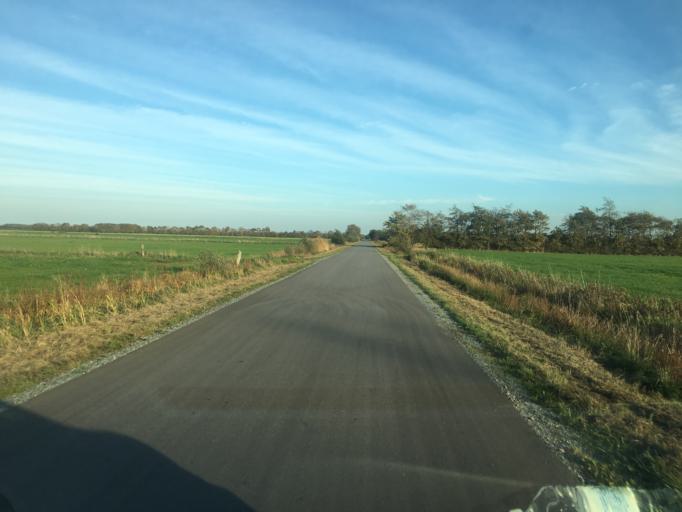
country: DE
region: Schleswig-Holstein
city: Ladelund
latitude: 54.8953
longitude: 9.0314
